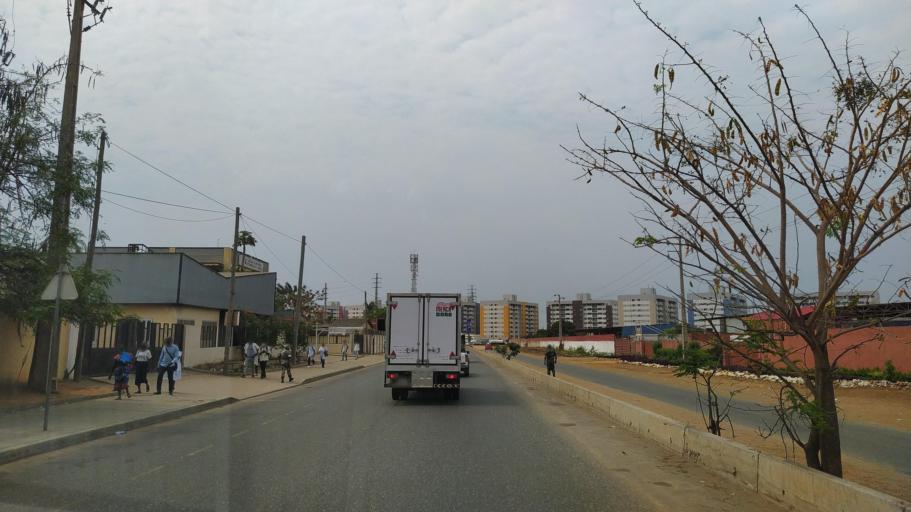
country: AO
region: Luanda
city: Luanda
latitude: -8.8544
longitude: 13.2888
